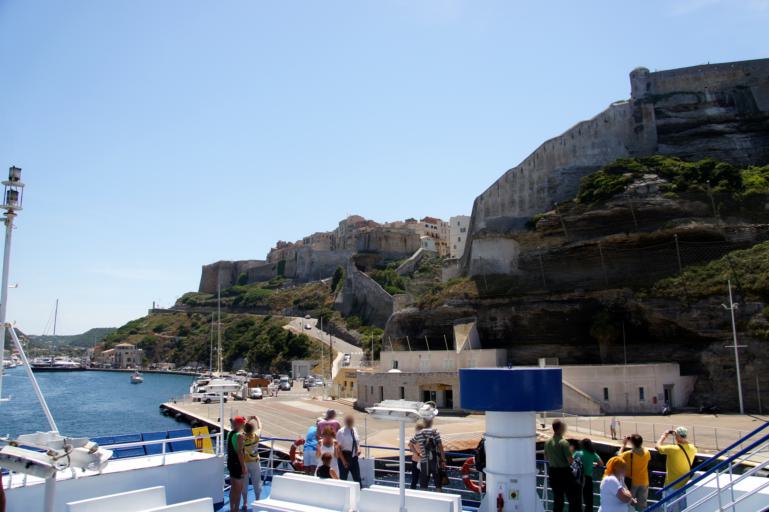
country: FR
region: Corsica
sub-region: Departement de la Corse-du-Sud
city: Bonifacio
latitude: 41.3890
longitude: 9.1499
